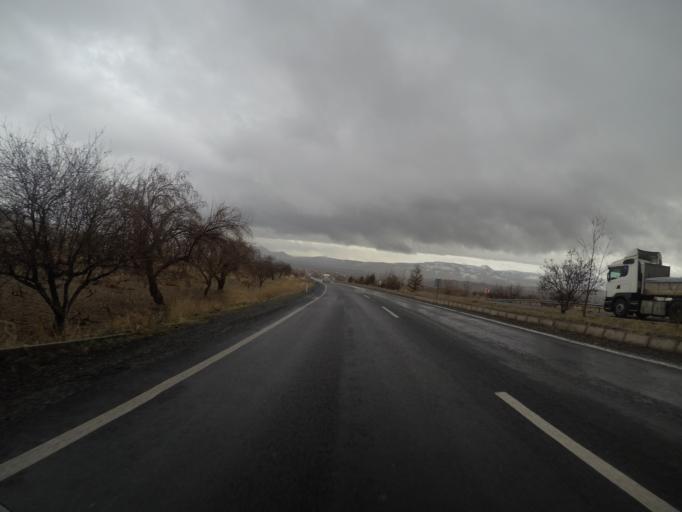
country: TR
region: Kayseri
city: Incesu
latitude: 38.6812
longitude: 35.2033
